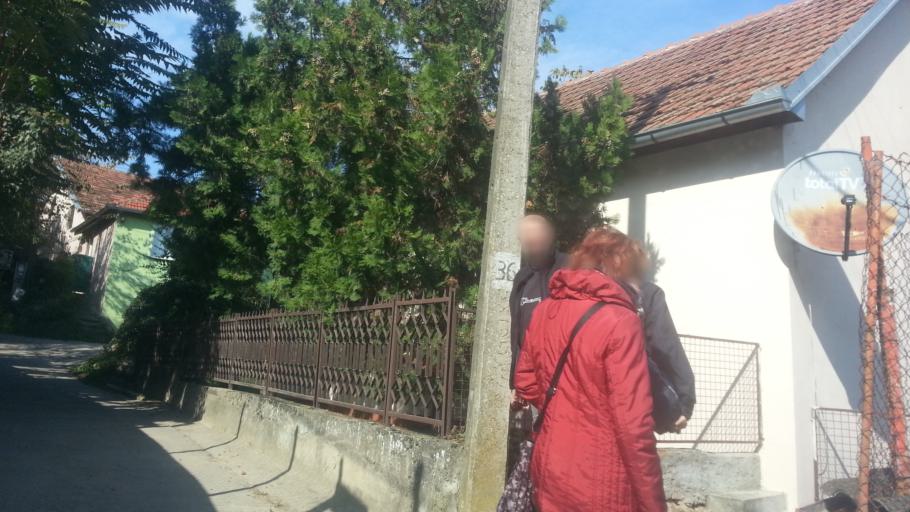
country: RS
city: Novi Slankamen
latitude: 45.1512
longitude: 20.2459
